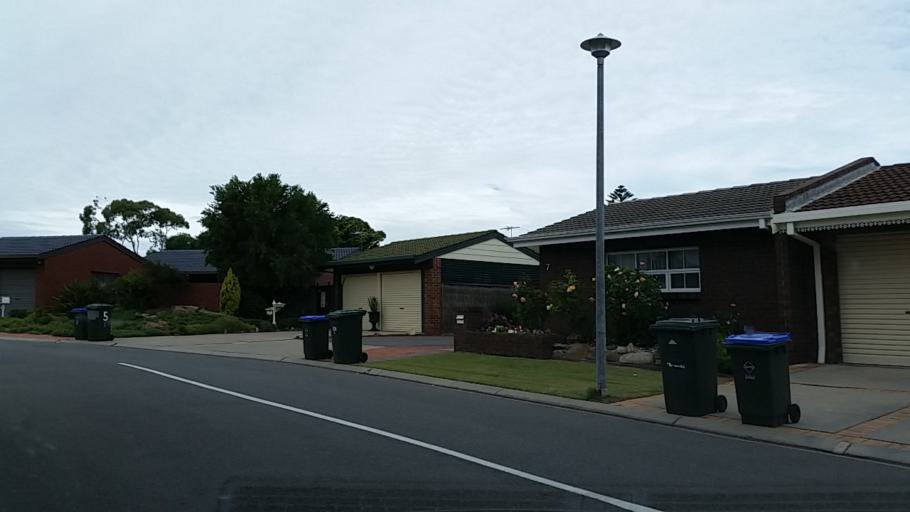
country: AU
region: South Australia
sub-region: Charles Sturt
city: West Lakes Shore
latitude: -34.8675
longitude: 138.4899
